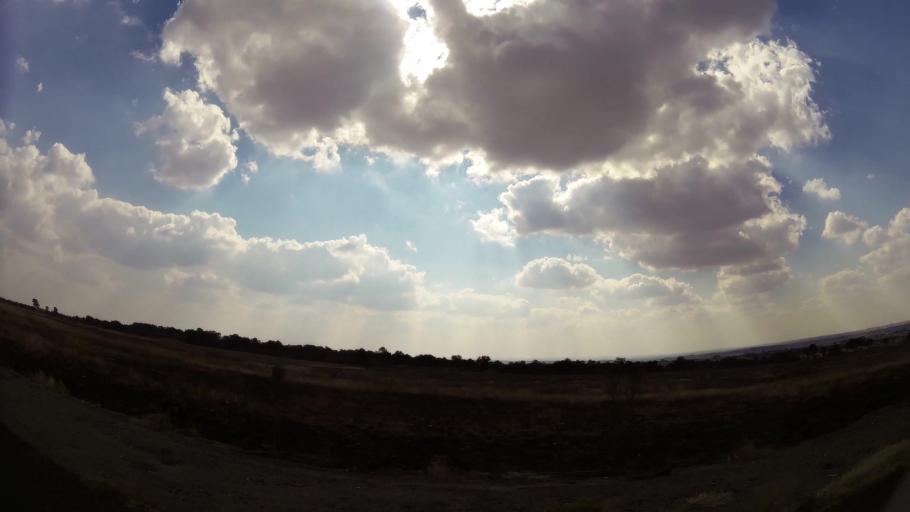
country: ZA
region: Mpumalanga
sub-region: Nkangala District Municipality
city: Delmas
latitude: -26.0941
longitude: 28.6700
